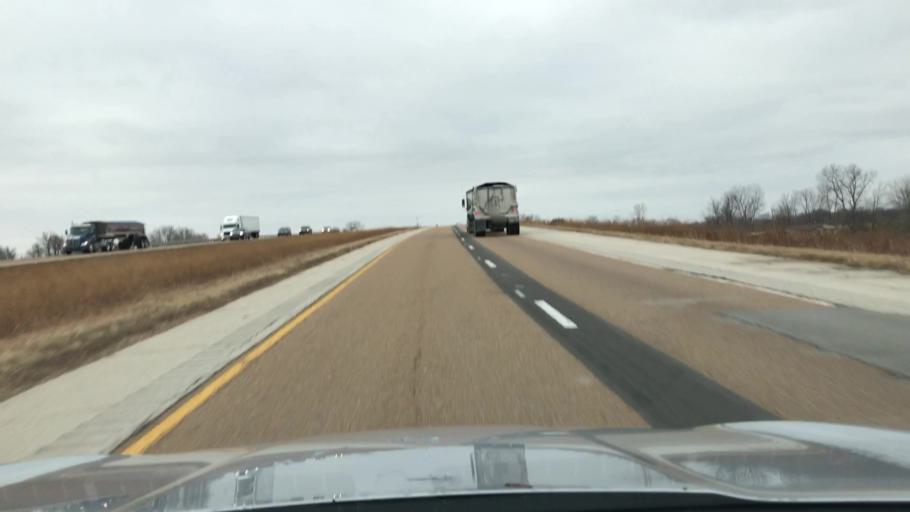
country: US
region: Illinois
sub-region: Montgomery County
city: Litchfield
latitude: 39.2201
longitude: -89.6484
